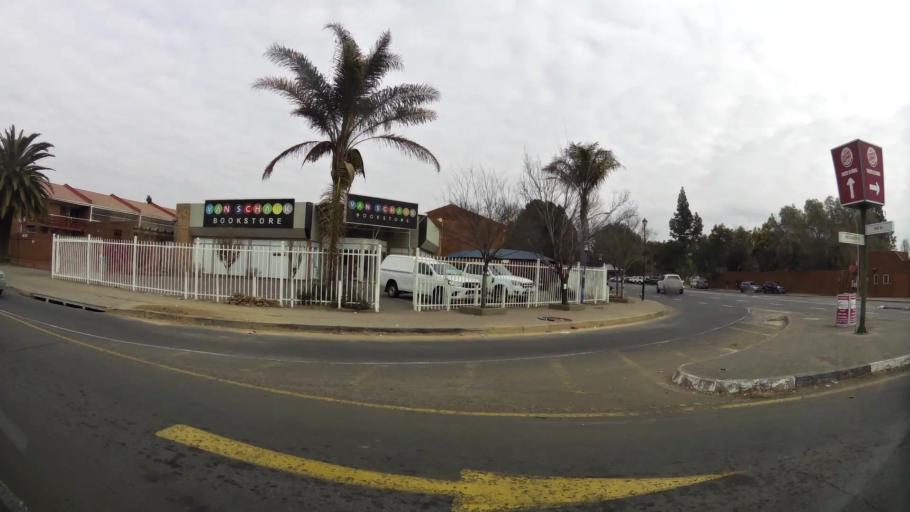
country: ZA
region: Orange Free State
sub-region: Mangaung Metropolitan Municipality
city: Bloemfontein
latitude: -29.1214
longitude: 26.2120
